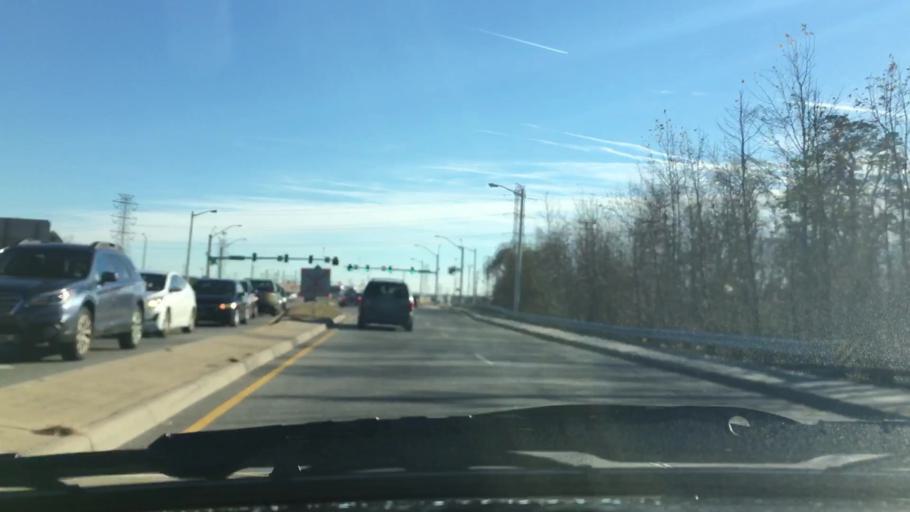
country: US
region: Virginia
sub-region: City of Portsmouth
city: Portsmouth Heights
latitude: 36.8810
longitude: -76.4253
